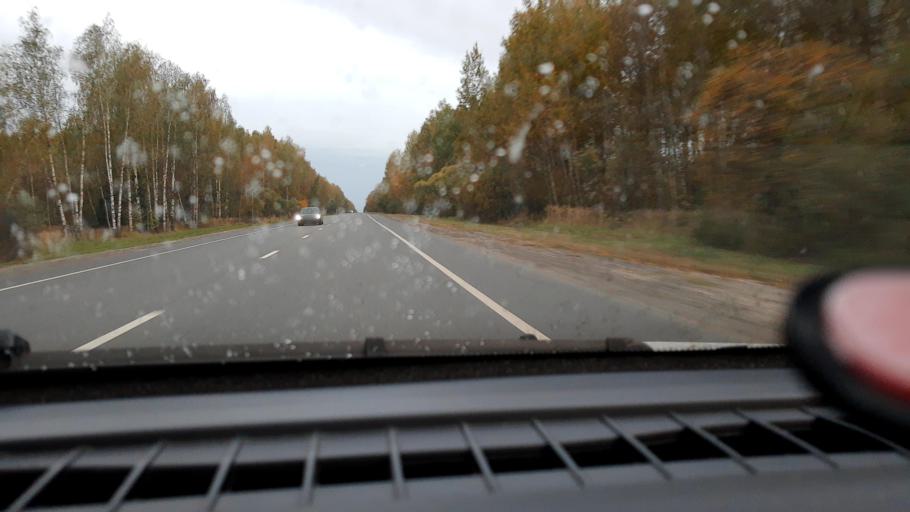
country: RU
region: Vladimir
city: Orgtrud
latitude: 56.2047
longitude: 40.7325
